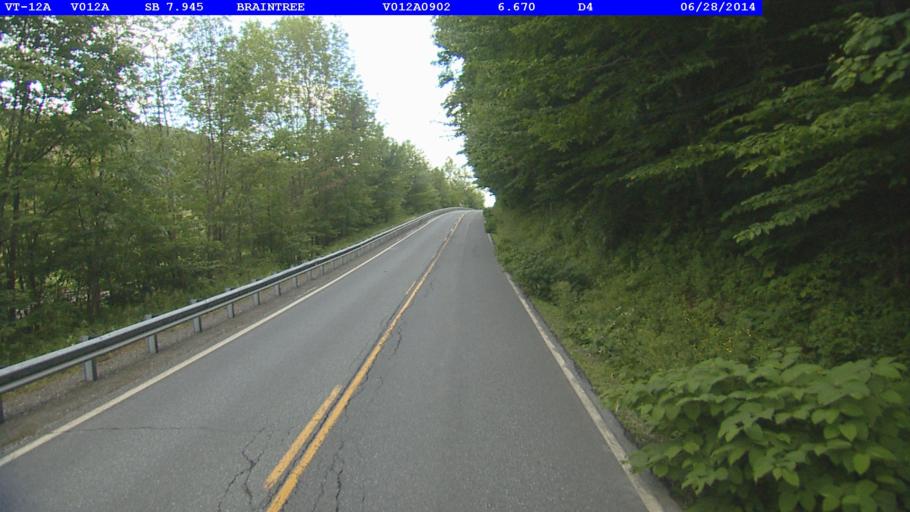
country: US
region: Vermont
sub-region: Orange County
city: Randolph
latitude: 44.0032
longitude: -72.7537
